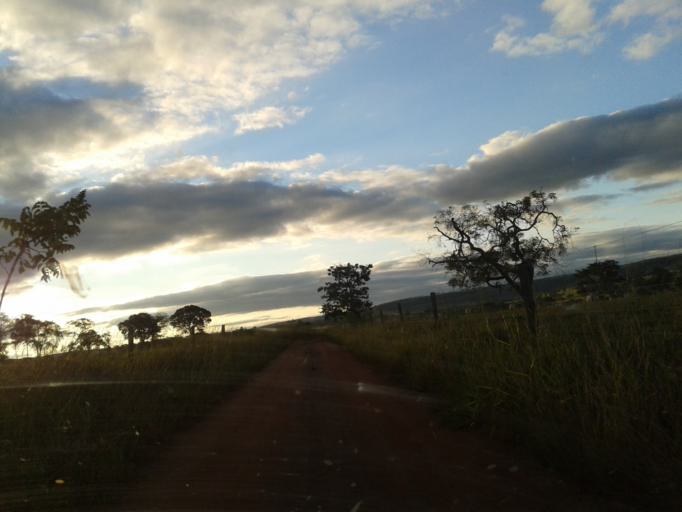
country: BR
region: Minas Gerais
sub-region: Campina Verde
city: Campina Verde
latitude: -19.5085
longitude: -49.6803
